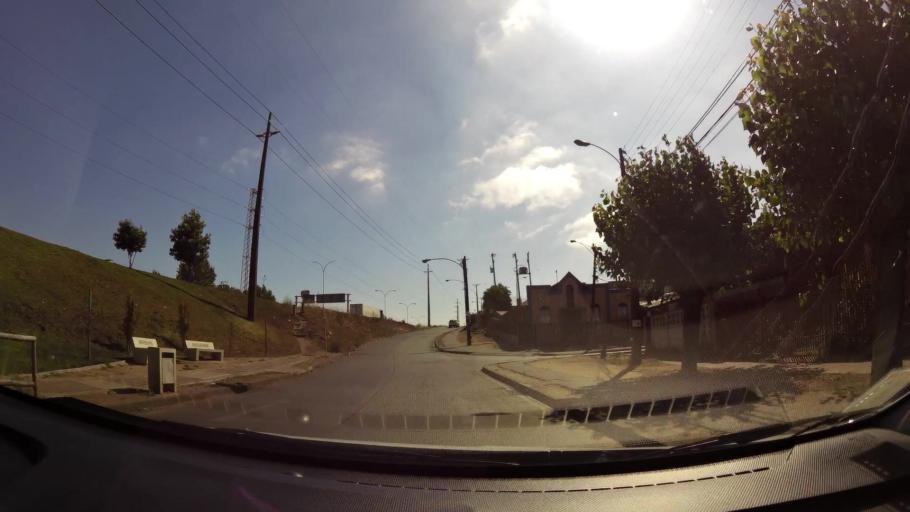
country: CL
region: Biobio
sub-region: Provincia de Concepcion
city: Concepcion
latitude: -36.7989
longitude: -73.0523
